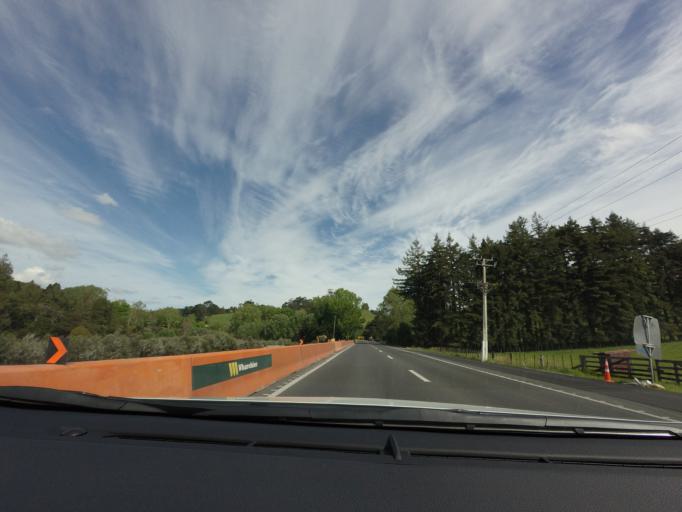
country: NZ
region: Auckland
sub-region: Auckland
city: Warkworth
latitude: -36.4414
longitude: 174.6498
